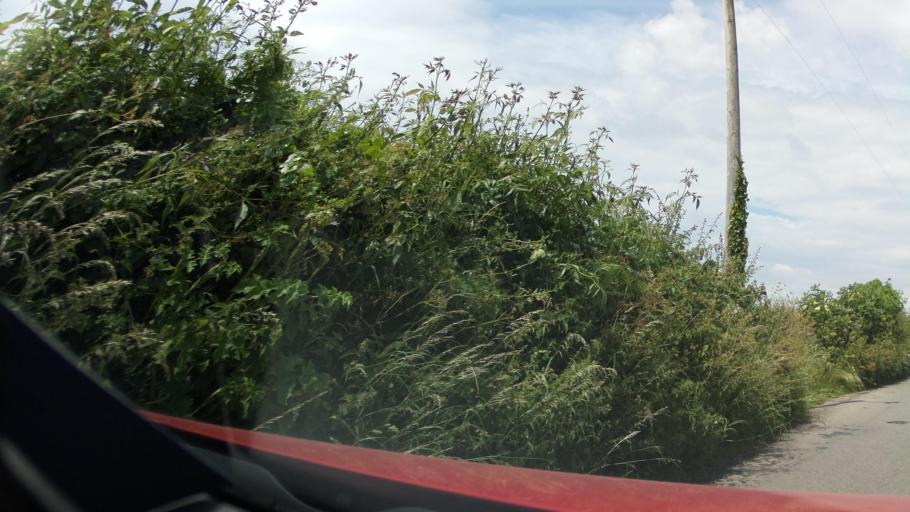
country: GB
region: Wales
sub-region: Vale of Glamorgan
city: Wick
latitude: 51.4374
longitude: -3.5676
